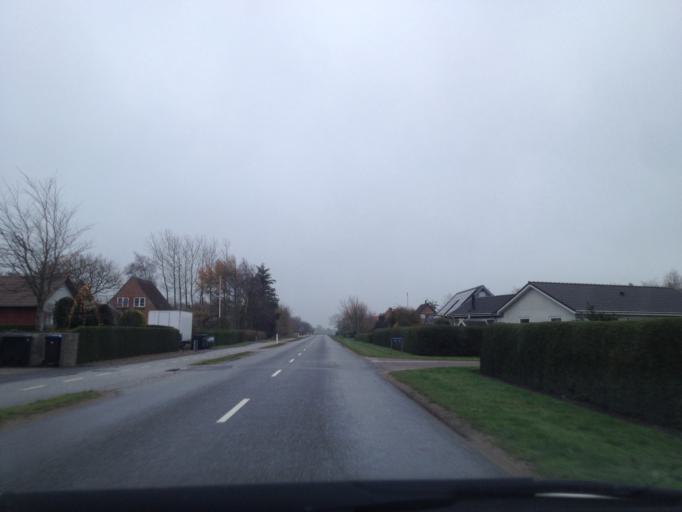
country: DK
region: South Denmark
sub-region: Tonder Kommune
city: Sherrebek
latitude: 55.1215
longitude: 8.7580
